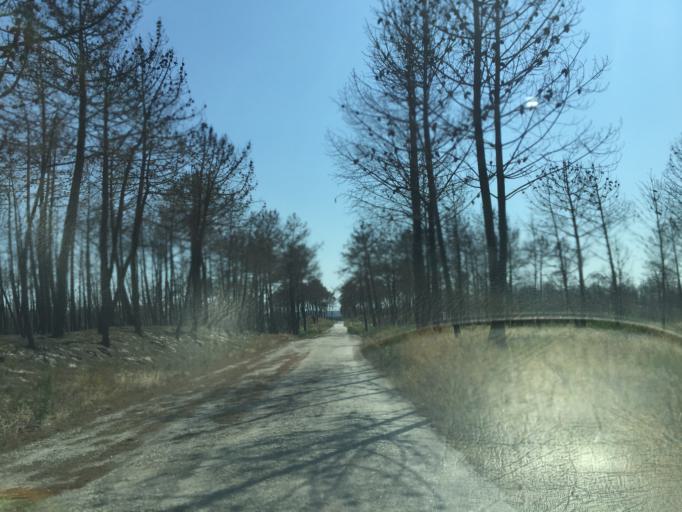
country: PT
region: Coimbra
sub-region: Figueira da Foz
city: Alhadas
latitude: 40.2668
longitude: -8.8321
